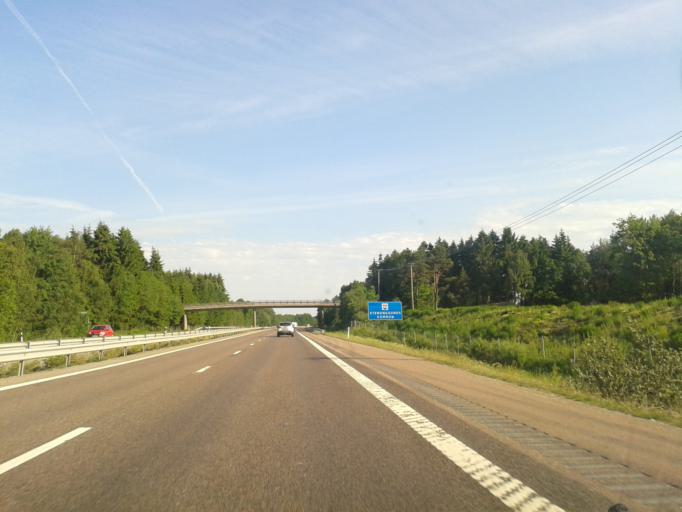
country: SE
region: Vaestra Goetaland
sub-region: Kungalvs Kommun
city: Kode
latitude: 57.9601
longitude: 11.8464
